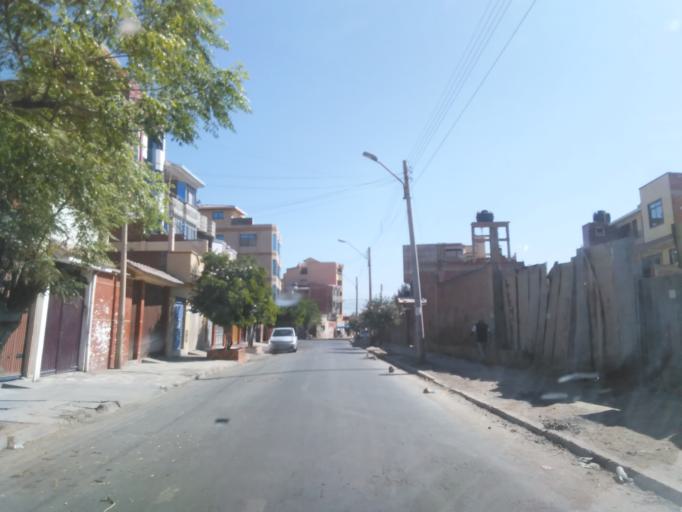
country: BO
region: Cochabamba
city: Cochabamba
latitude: -17.4146
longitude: -66.1559
